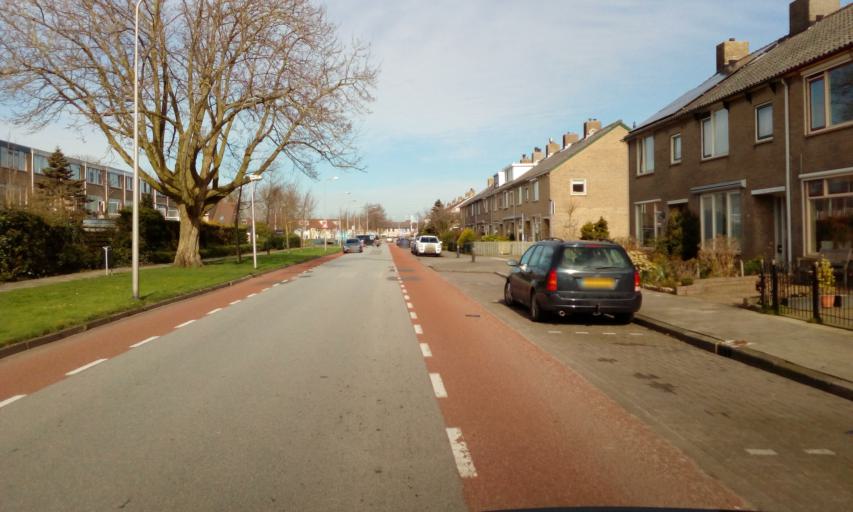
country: NL
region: South Holland
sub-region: Gemeente Nieuwkoop
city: Nieuwkoop
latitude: 52.1499
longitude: 4.7718
